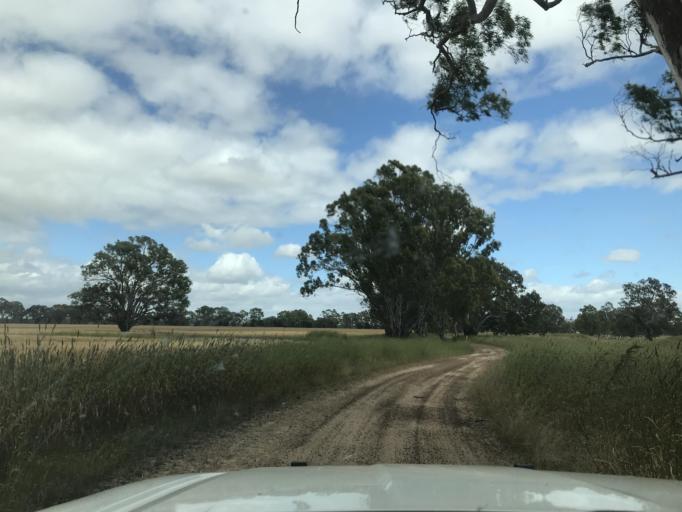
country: AU
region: South Australia
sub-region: Naracoorte and Lucindale
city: Naracoorte
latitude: -36.9000
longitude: 141.3975
